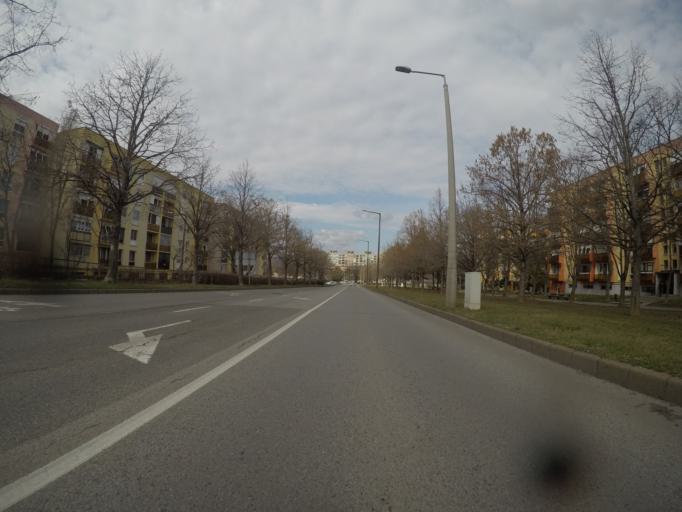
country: HU
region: Baranya
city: Pecs
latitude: 46.0444
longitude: 18.2258
